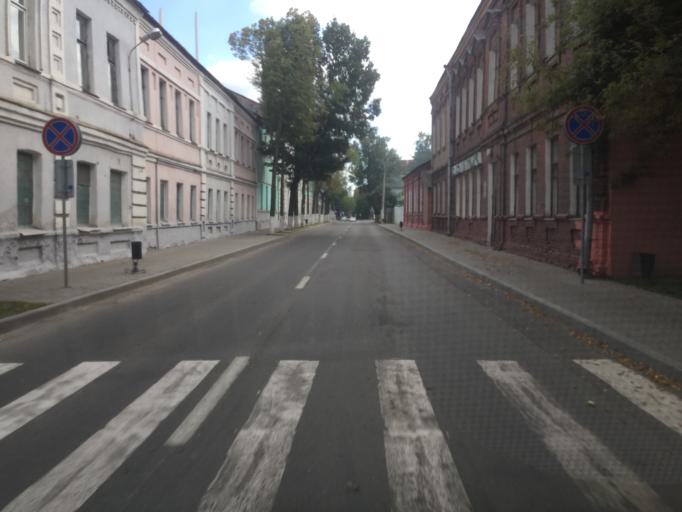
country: BY
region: Vitebsk
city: Vitebsk
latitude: 55.1987
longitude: 30.1909
